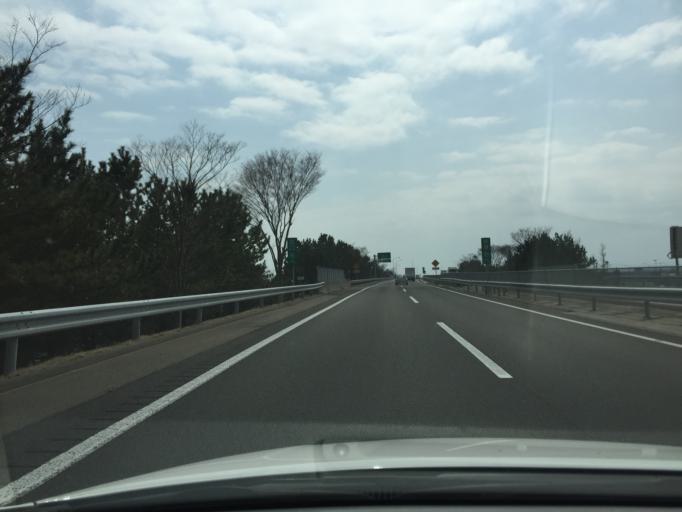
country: JP
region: Miyagi
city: Iwanuma
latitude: 38.1110
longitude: 140.8893
